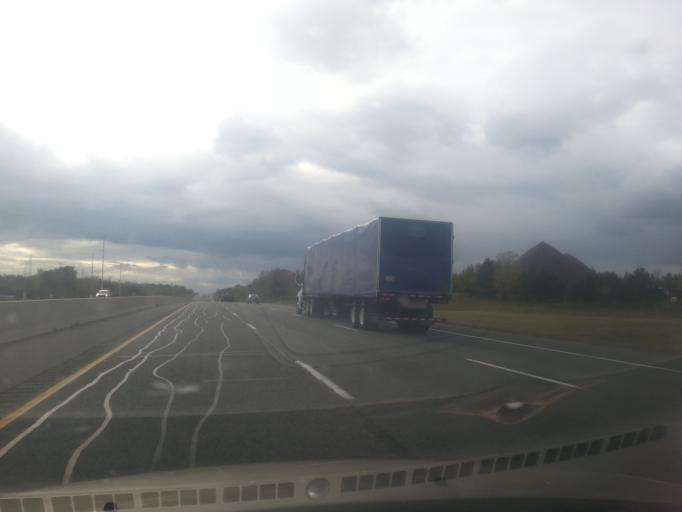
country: CA
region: Ontario
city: Cobourg
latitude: 43.9310
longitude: -78.4898
